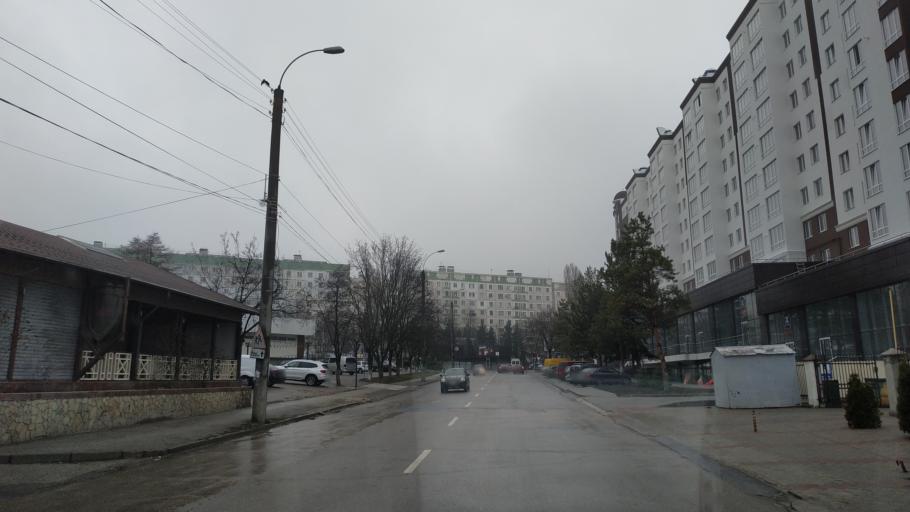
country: MD
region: Chisinau
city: Vatra
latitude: 47.0425
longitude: 28.7720
